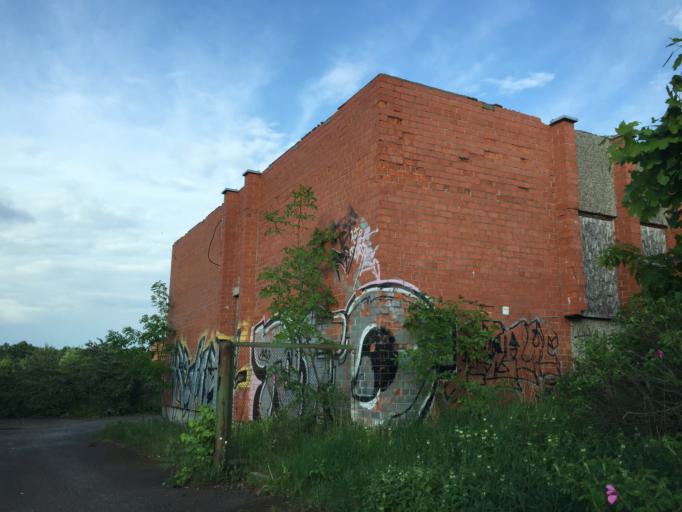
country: LT
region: Klaipedos apskritis
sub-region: Klaipeda
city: Klaipeda
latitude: 55.7541
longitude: 21.1330
